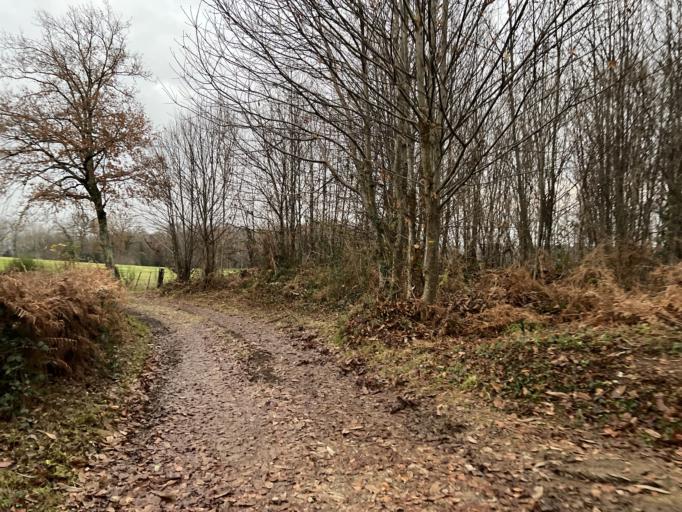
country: FR
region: Limousin
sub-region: Departement de la Correze
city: Sainte-Fortunade
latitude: 45.2196
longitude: 1.7789
